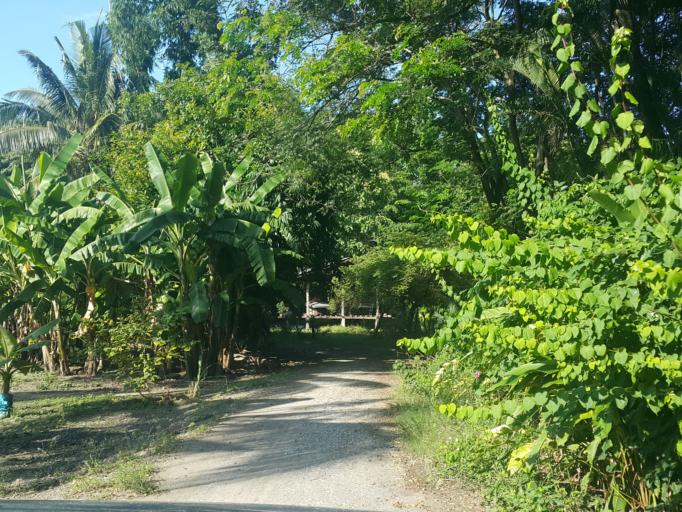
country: TH
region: Chiang Mai
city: San Kamphaeng
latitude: 18.7187
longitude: 99.1808
